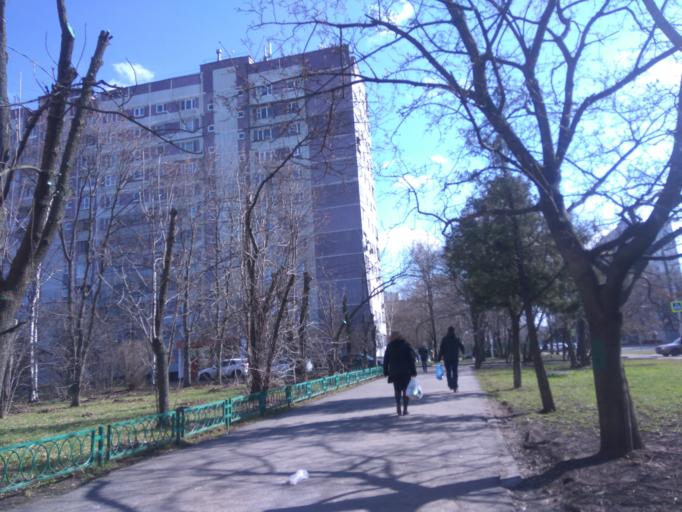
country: RU
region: Moscow
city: Ivanovskoye
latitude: 55.7620
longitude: 37.8328
